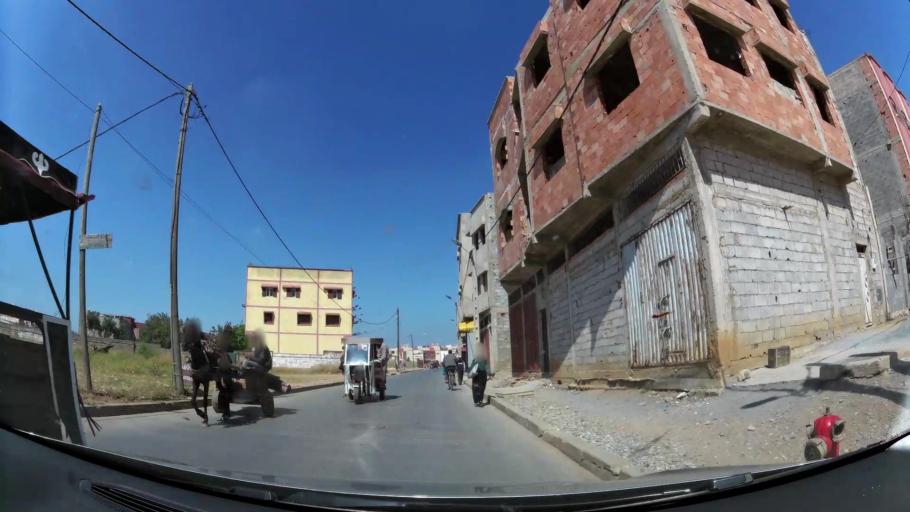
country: MA
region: Rabat-Sale-Zemmour-Zaer
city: Sale
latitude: 34.0692
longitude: -6.7582
